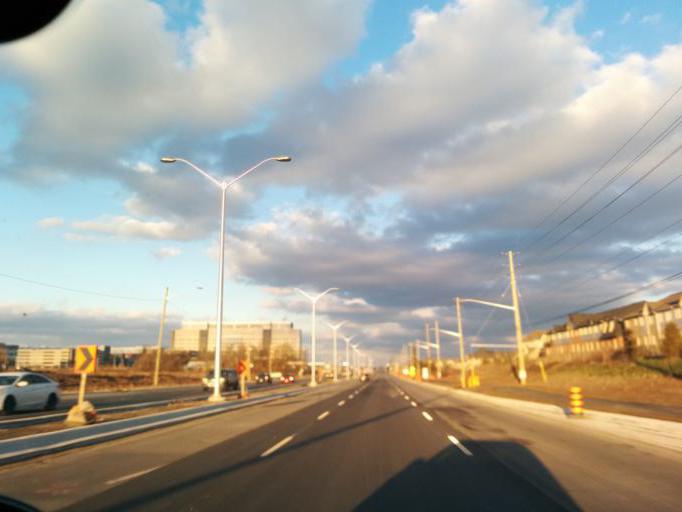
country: CA
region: Ontario
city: Oakville
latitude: 43.4443
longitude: -79.7671
